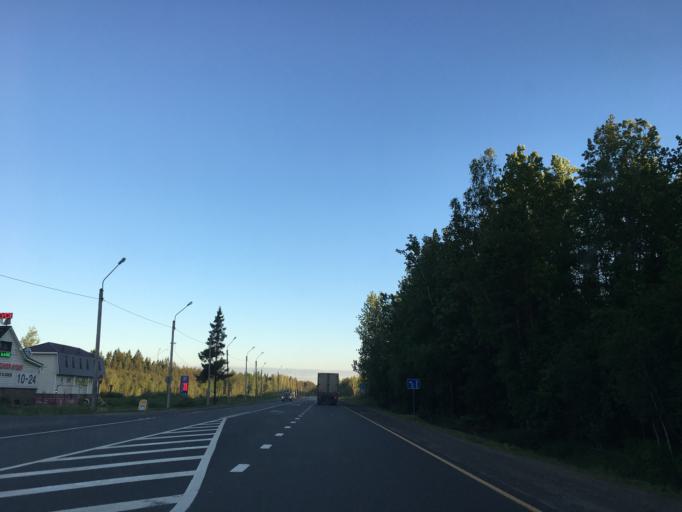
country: RU
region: Leningrad
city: Rozhdestveno
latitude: 59.3031
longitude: 29.9420
